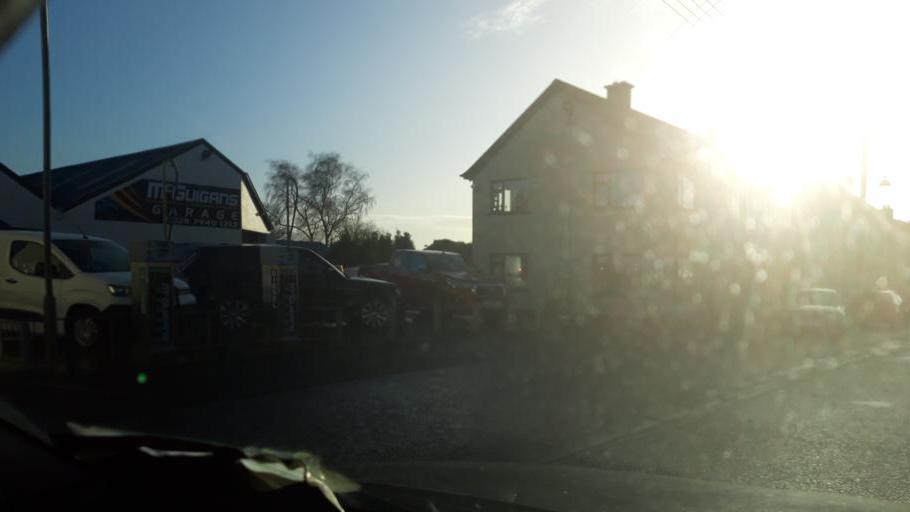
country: GB
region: Northern Ireland
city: Maghera
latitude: 54.9096
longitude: -6.6642
